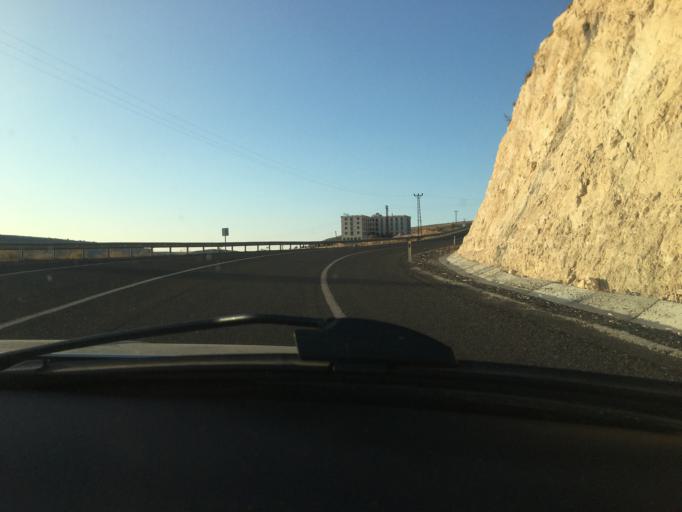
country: TR
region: Sanliurfa
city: Halfeti
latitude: 37.2446
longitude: 37.8732
